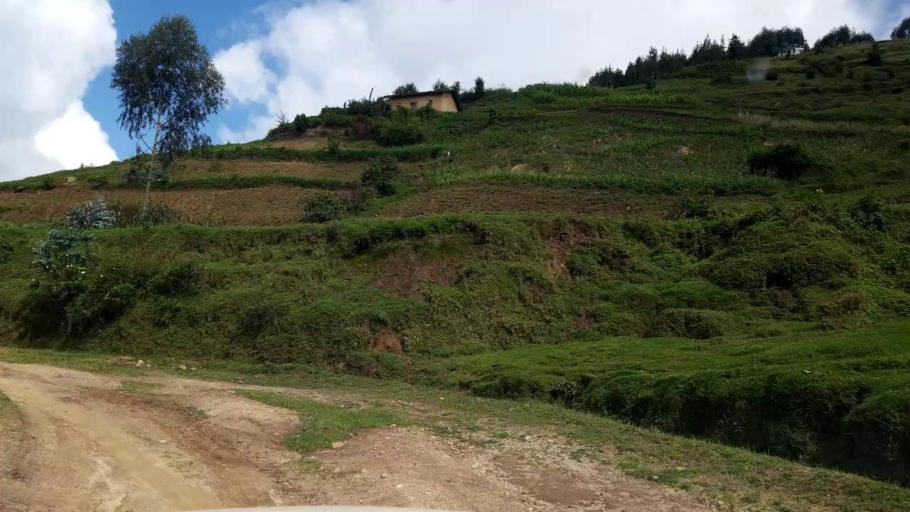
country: RW
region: Western Province
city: Kibuye
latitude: -1.8810
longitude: 29.4759
